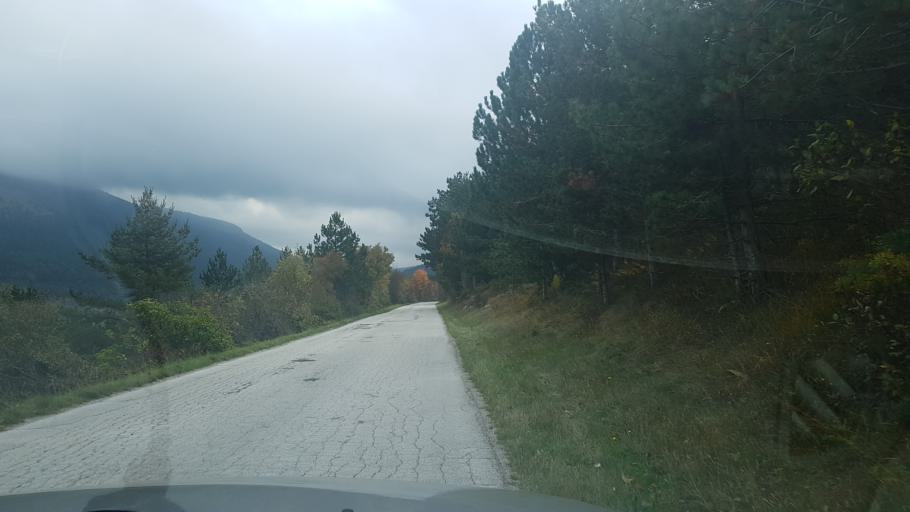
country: HR
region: Istarska
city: Buzet
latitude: 45.4944
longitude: 14.0262
